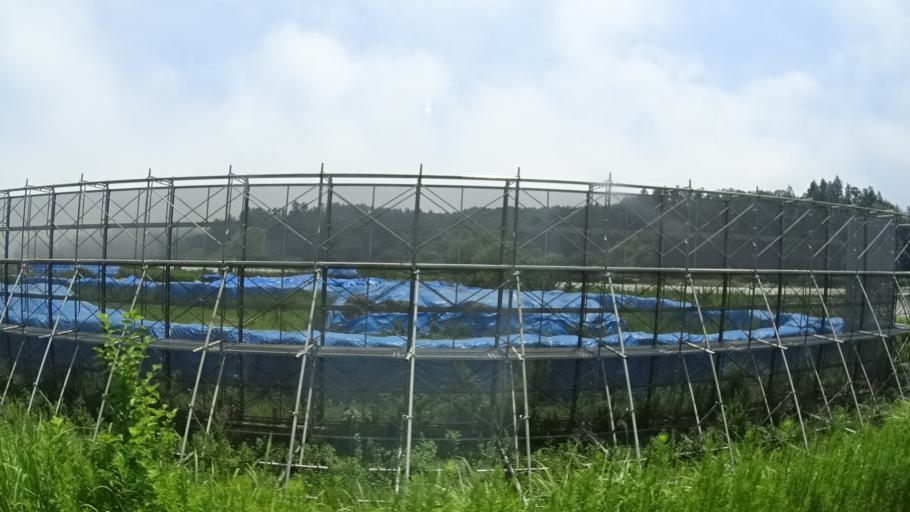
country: JP
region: Fukushima
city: Namie
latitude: 37.3245
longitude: 141.0180
